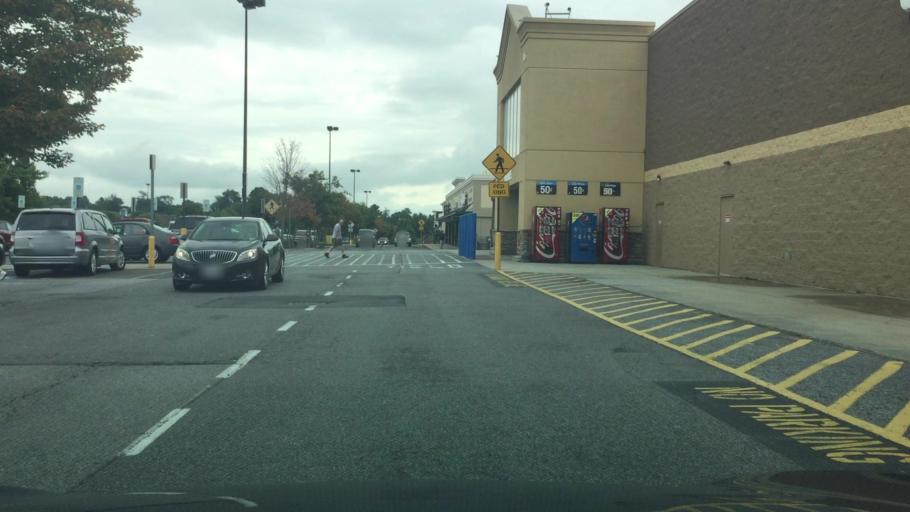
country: US
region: Virginia
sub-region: Wythe County
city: Wytheville
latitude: 36.9568
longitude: -81.0993
